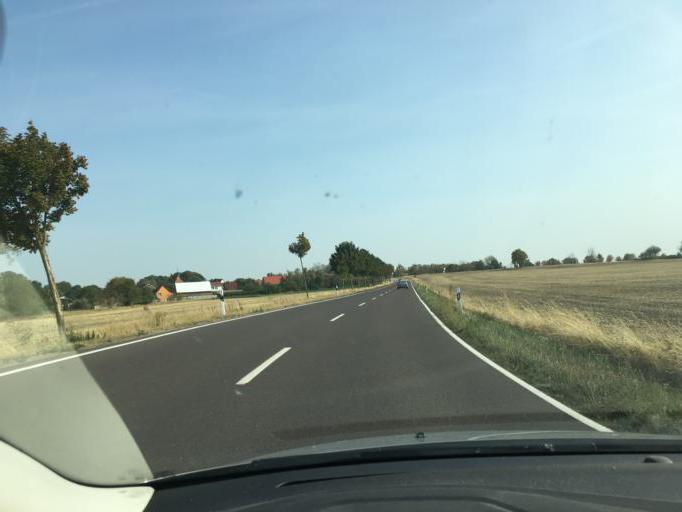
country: DE
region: Saxony-Anhalt
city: Wulfen
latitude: 51.7765
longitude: 11.9031
